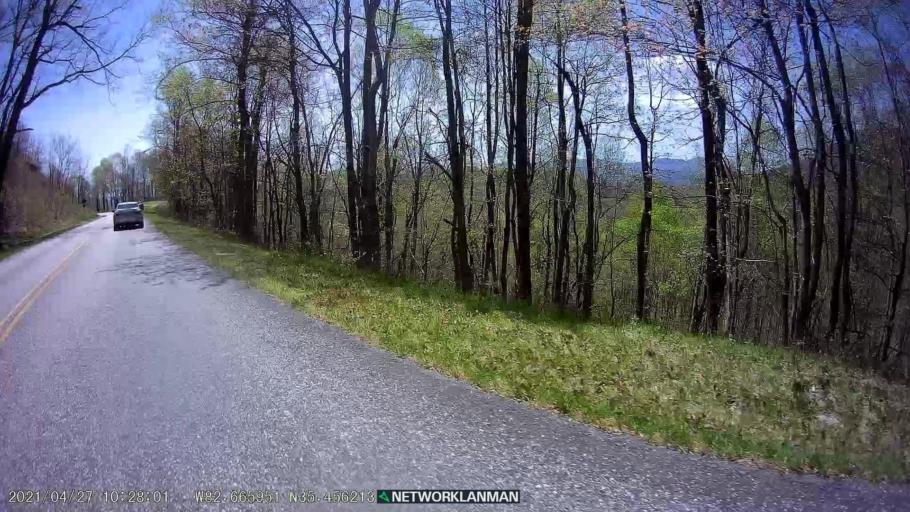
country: US
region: North Carolina
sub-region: Buncombe County
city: Bent Creek
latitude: 35.4556
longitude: -82.6660
